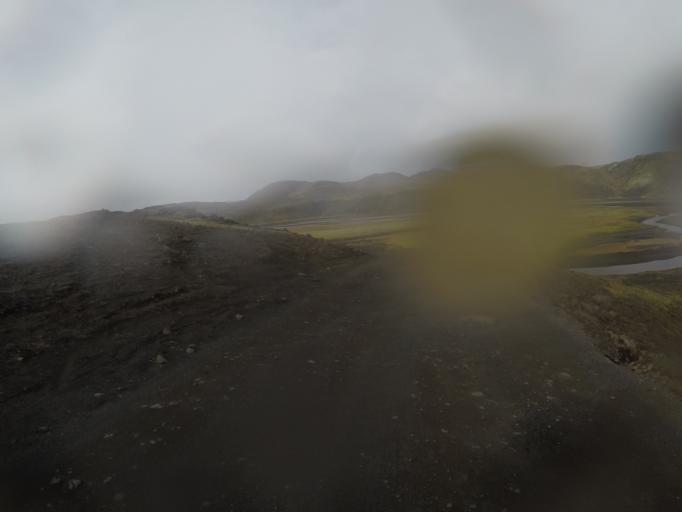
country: IS
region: South
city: Vestmannaeyjar
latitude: 63.9826
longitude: -18.8557
